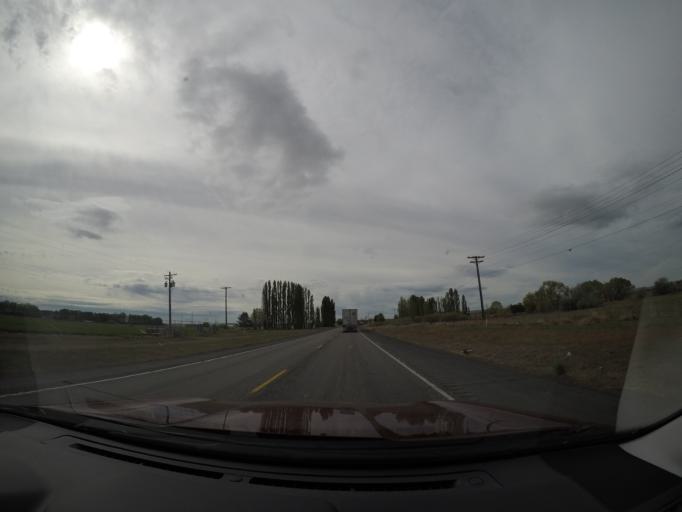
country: US
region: Washington
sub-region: Grant County
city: Quincy
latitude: 47.0965
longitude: -119.8535
